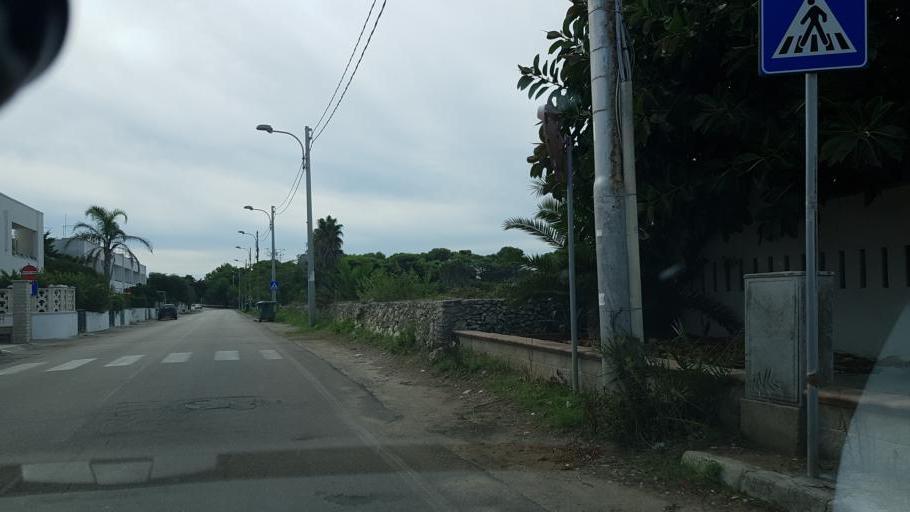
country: IT
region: Apulia
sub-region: Provincia di Lecce
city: Borgagne
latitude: 40.2910
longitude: 18.4230
